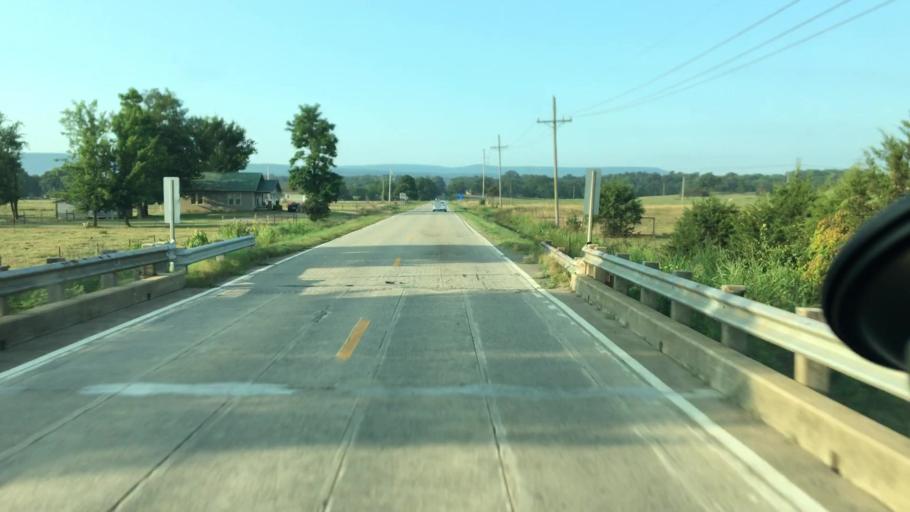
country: US
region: Arkansas
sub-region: Logan County
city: Paris
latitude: 35.3250
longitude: -93.6322
